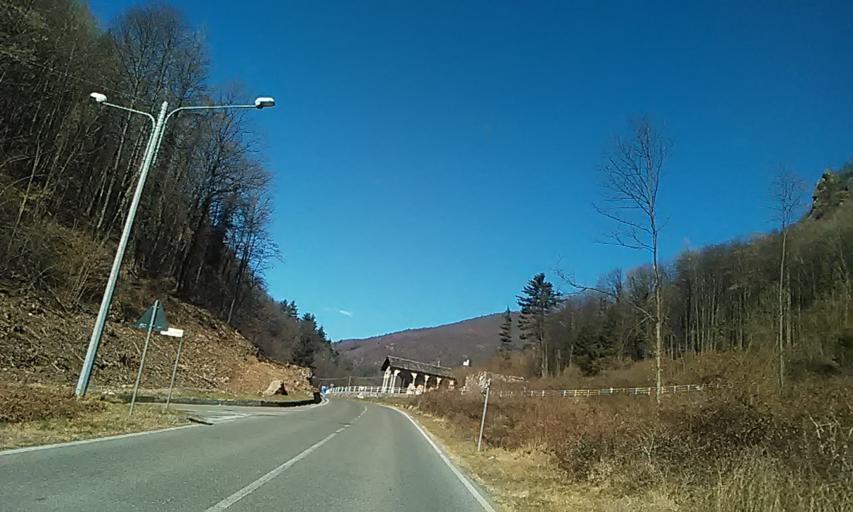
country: IT
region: Piedmont
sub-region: Provincia di Vercelli
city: Varallo
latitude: 45.8042
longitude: 8.2731
